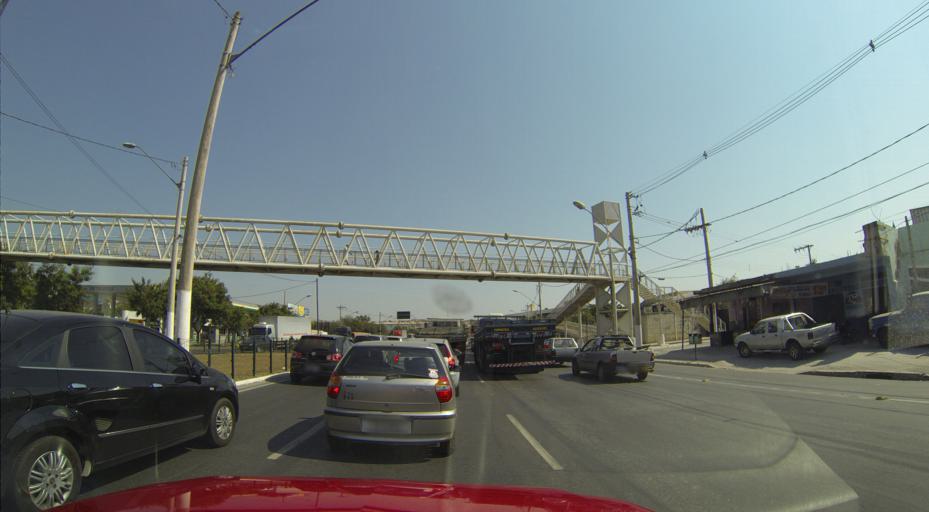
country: BR
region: Minas Gerais
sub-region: Belo Horizonte
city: Belo Horizonte
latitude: -19.8605
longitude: -43.9333
